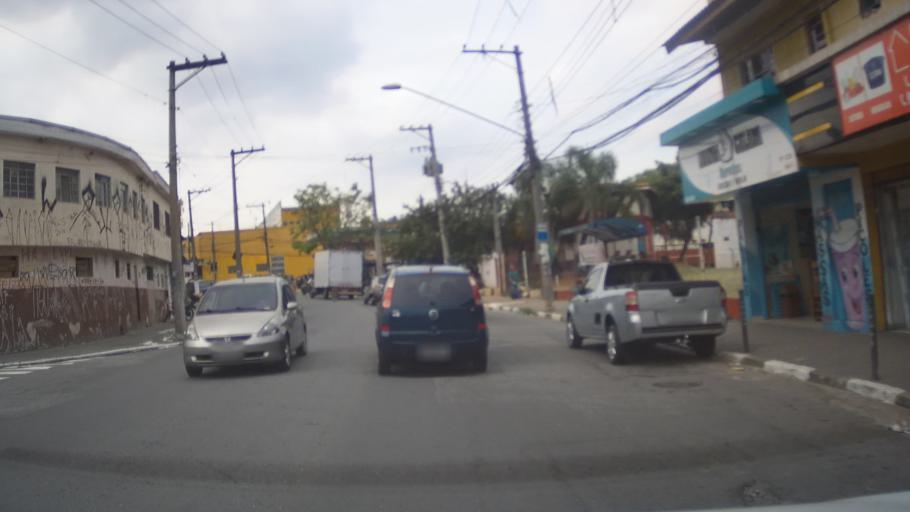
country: BR
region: Sao Paulo
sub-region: Guarulhos
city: Guarulhos
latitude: -23.4280
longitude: -46.5089
